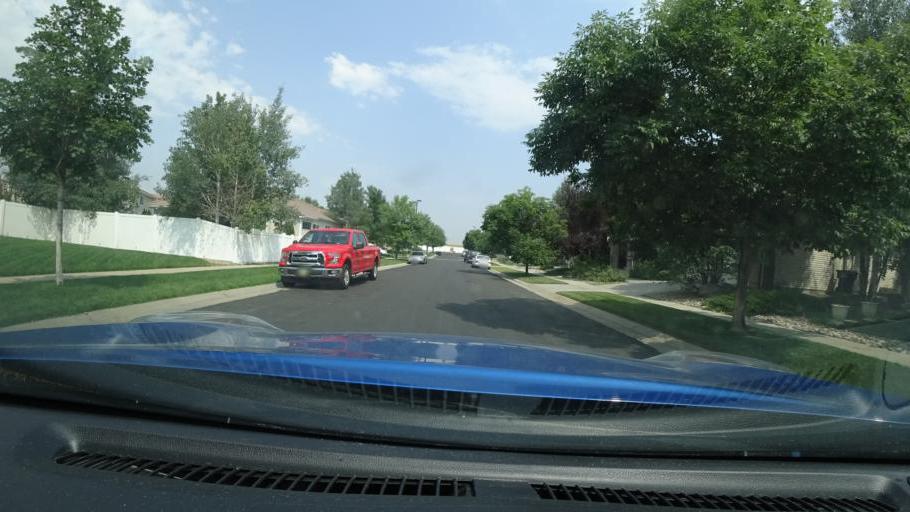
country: US
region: Colorado
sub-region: Adams County
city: Aurora
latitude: 39.7824
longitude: -104.7364
